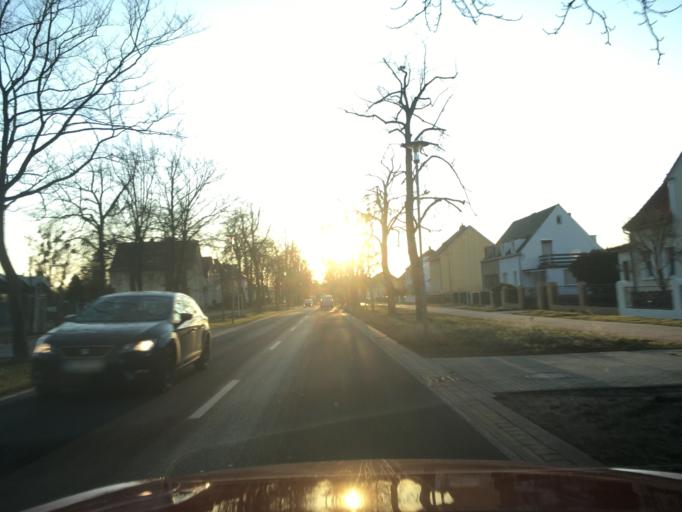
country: DE
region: Saxony-Anhalt
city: Rosslau
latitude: 51.8907
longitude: 12.2609
